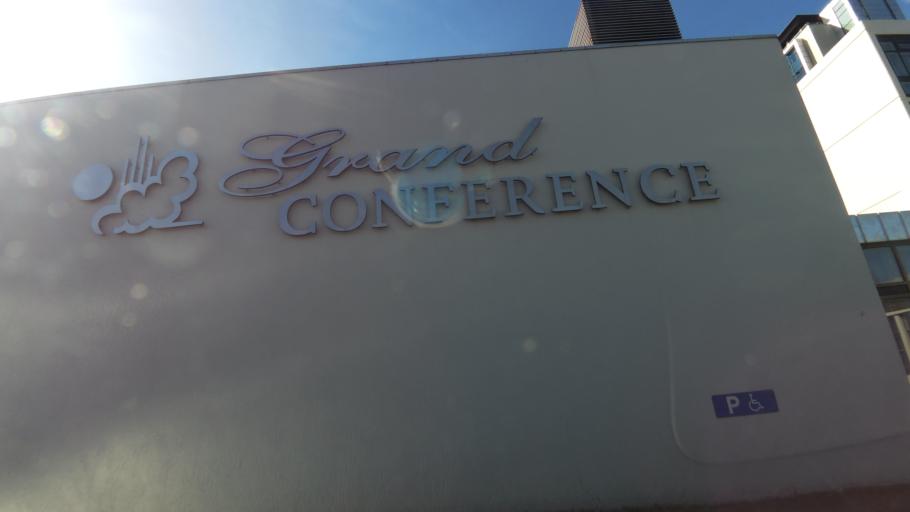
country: IS
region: Capital Region
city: Reykjavik
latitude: 64.1424
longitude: -21.8903
